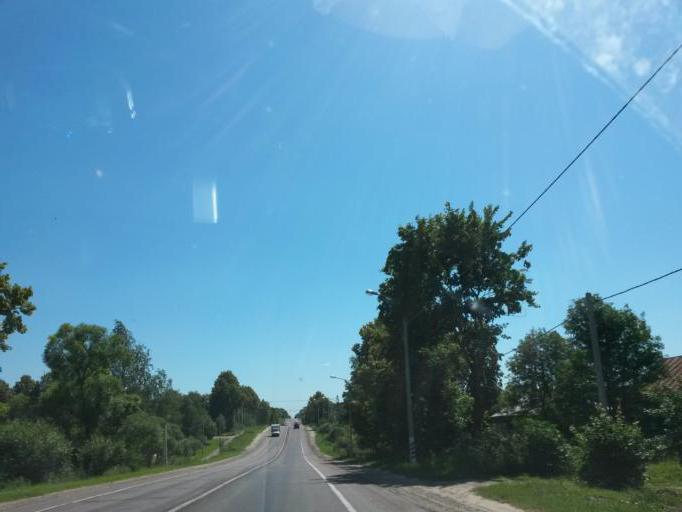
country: RU
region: Moskovskaya
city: Proletarskiy
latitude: 55.0718
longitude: 37.4377
